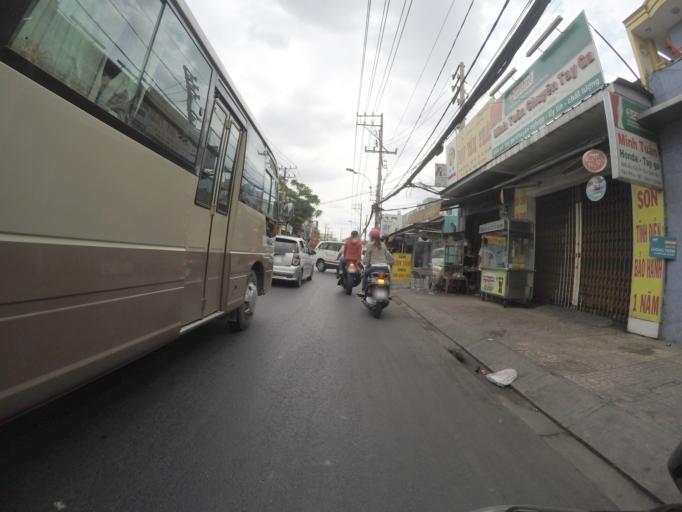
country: VN
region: Ho Chi Minh City
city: Quan Tan Phu
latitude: 10.7994
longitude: 106.6372
